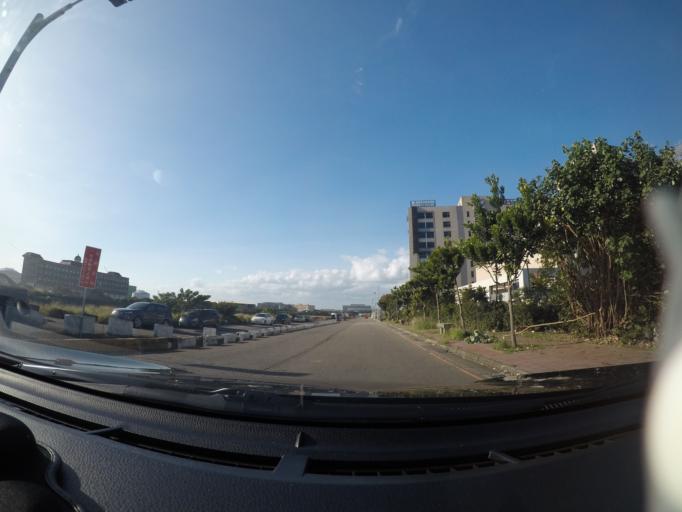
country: TW
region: Taiwan
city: Taoyuan City
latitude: 25.0920
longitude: 121.2537
